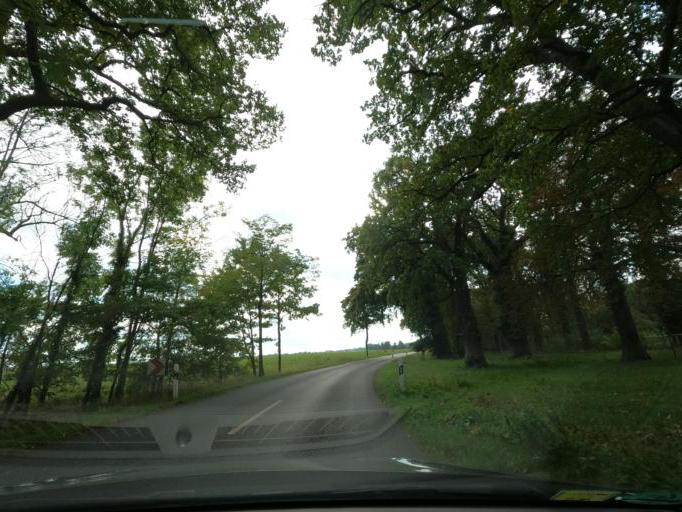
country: DE
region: Lower Saxony
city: Adenbuettel
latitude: 52.3723
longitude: 10.4369
